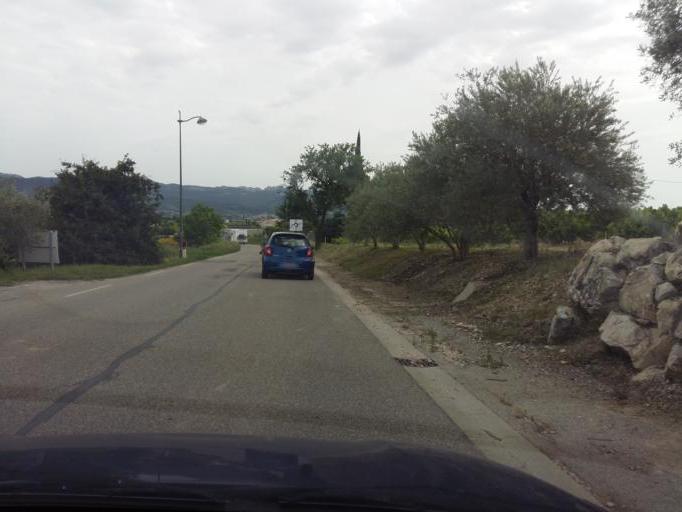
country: FR
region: Provence-Alpes-Cote d'Azur
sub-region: Departement du Vaucluse
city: Sablet
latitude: 44.2269
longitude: 4.9870
